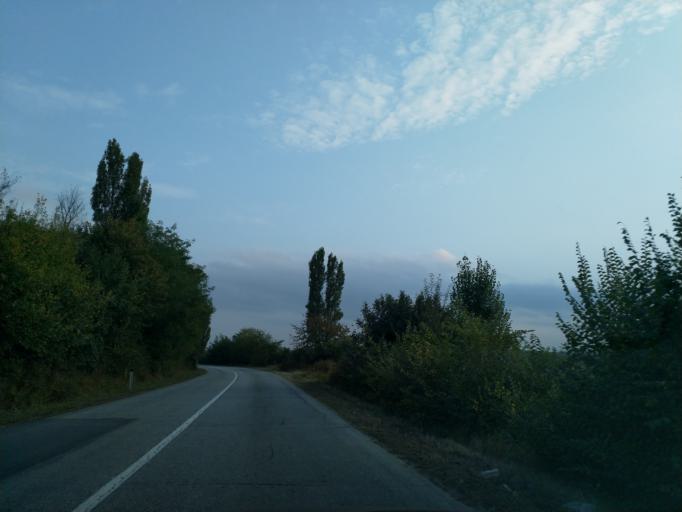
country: RS
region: Central Serbia
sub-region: Sumadijski Okrug
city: Topola
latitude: 44.1946
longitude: 20.7343
